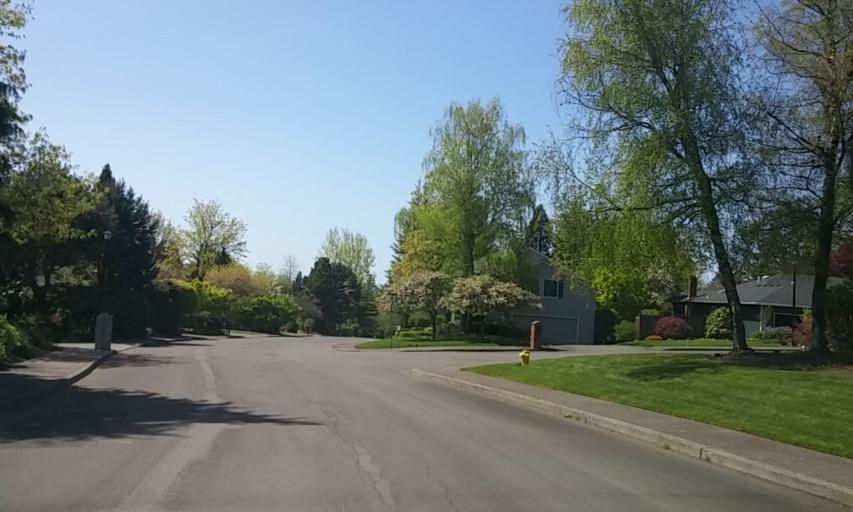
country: US
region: Oregon
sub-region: Washington County
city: West Haven
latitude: 45.5257
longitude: -122.7657
